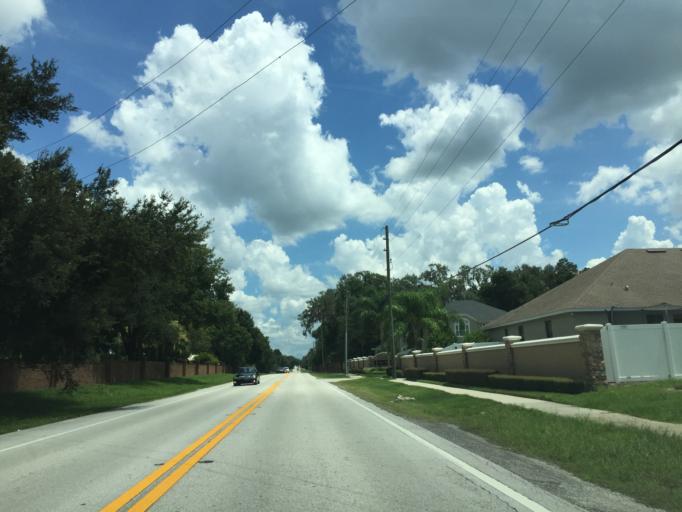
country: US
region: Florida
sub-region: Orange County
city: Alafaya
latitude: 28.6118
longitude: -81.2232
